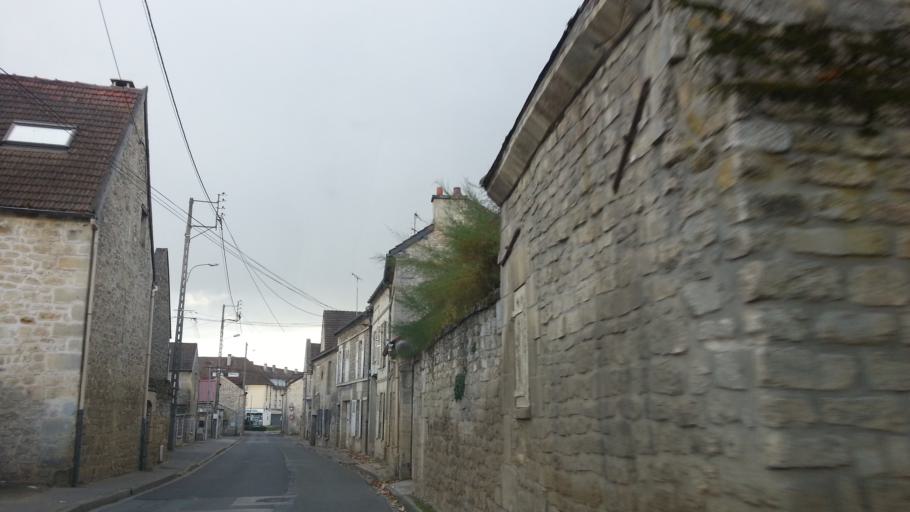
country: FR
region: Picardie
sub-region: Departement de l'Oise
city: Villers-sous-Saint-Leu
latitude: 49.2183
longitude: 2.4162
